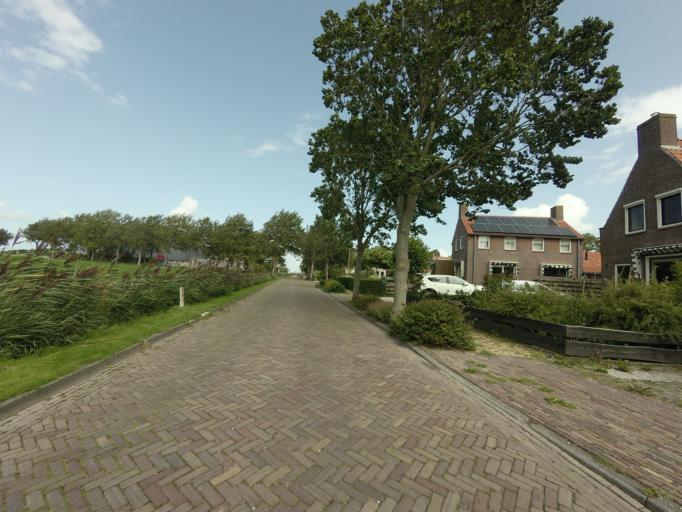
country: NL
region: Friesland
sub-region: Gemeente Harlingen
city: Harlingen
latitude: 53.1165
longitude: 5.4377
